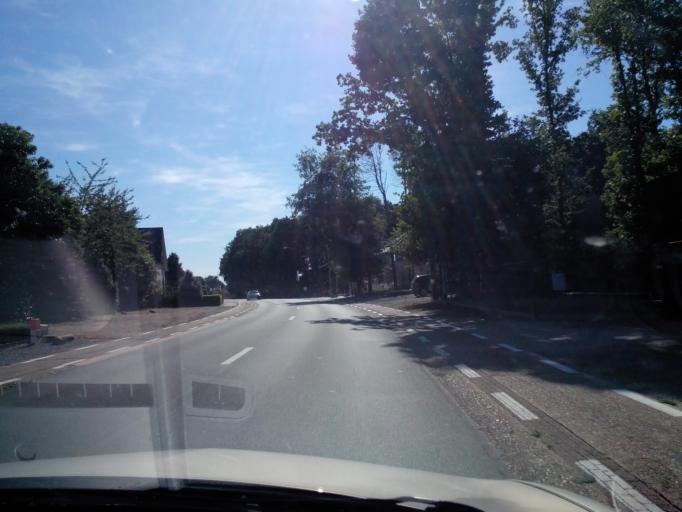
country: BE
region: Flanders
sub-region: Provincie Limburg
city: Opglabbeek
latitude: 51.0393
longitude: 5.5658
